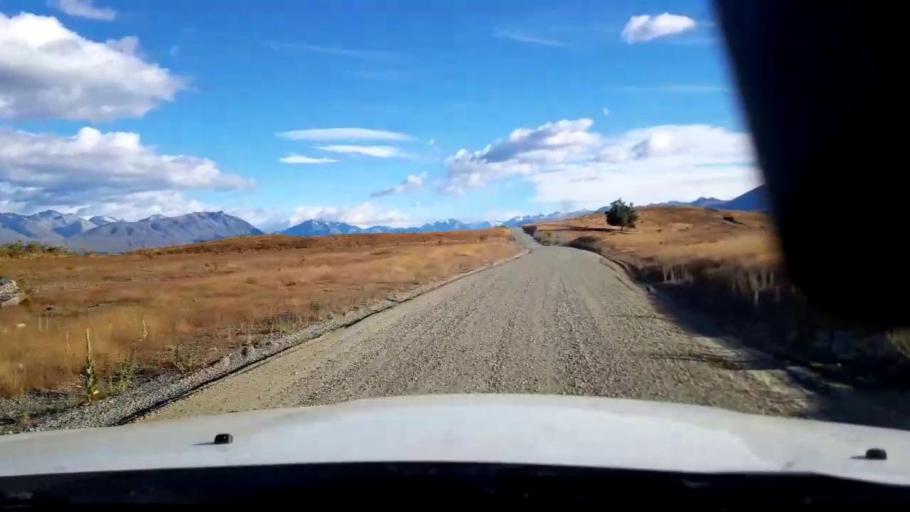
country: NZ
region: Canterbury
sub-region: Timaru District
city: Pleasant Point
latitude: -43.9762
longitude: 170.5112
